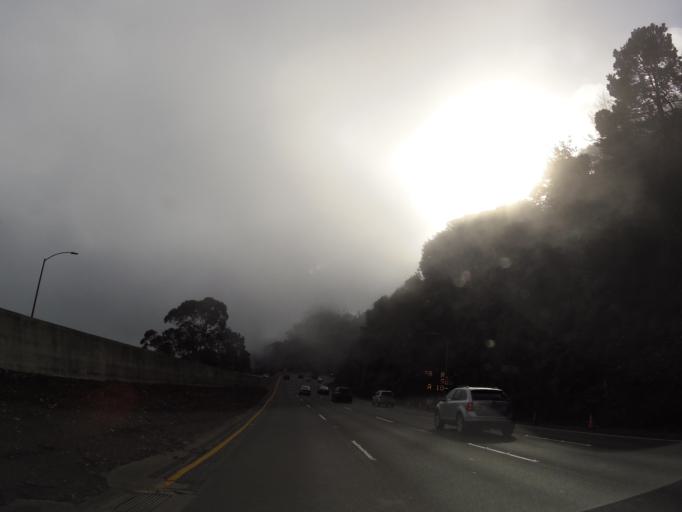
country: US
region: California
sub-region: Marin County
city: Sausalito
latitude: 37.8483
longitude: -122.4890
